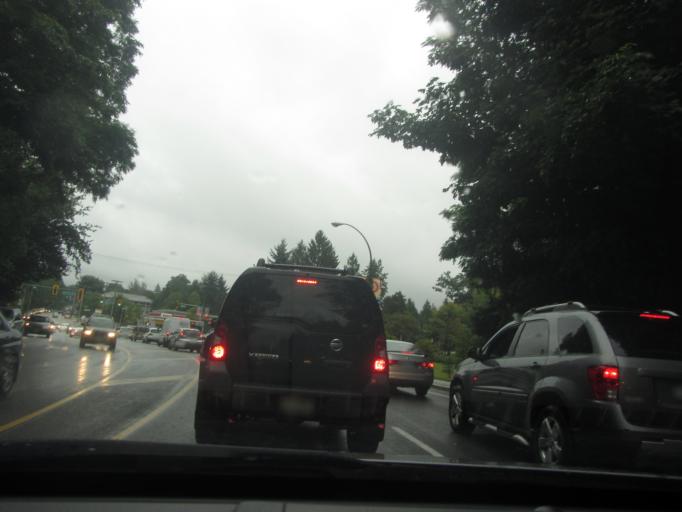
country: CA
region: British Columbia
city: Burnaby
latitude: 49.2402
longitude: -122.9661
